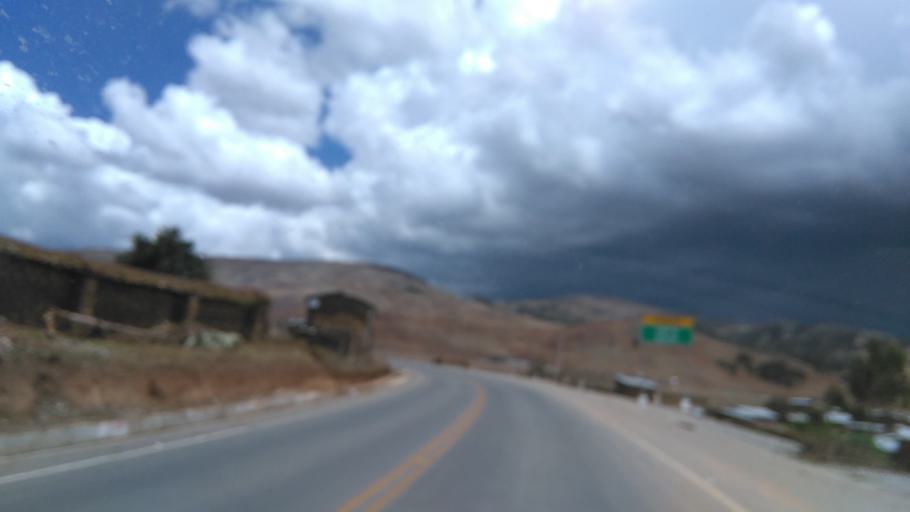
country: PE
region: Apurimac
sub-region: Provincia de Andahuaylas
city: San Jeronimo
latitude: -13.7020
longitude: -73.3549
